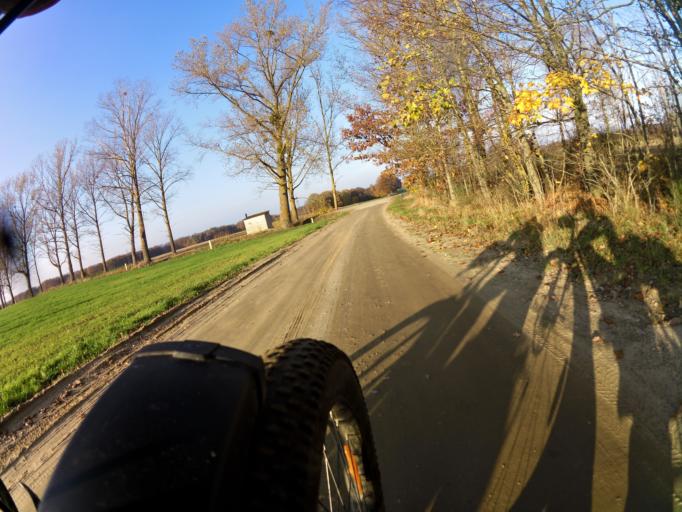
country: PL
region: Pomeranian Voivodeship
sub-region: Powiat pucki
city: Krokowa
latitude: 54.7350
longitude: 18.1957
